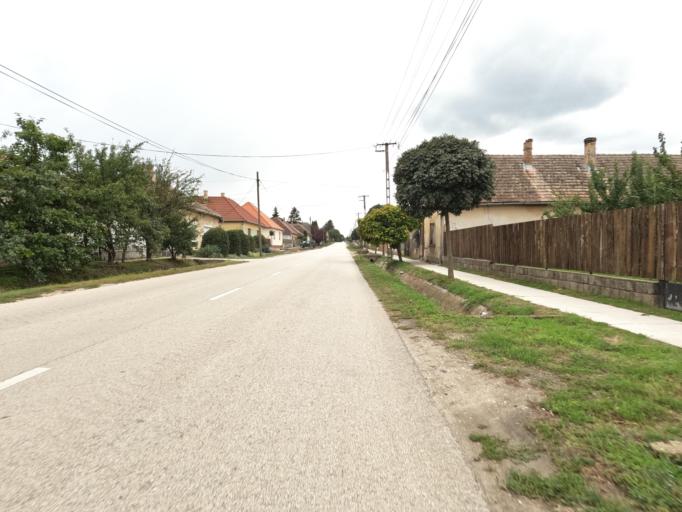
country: HU
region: Tolna
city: Tengelic
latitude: 46.5344
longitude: 18.7087
